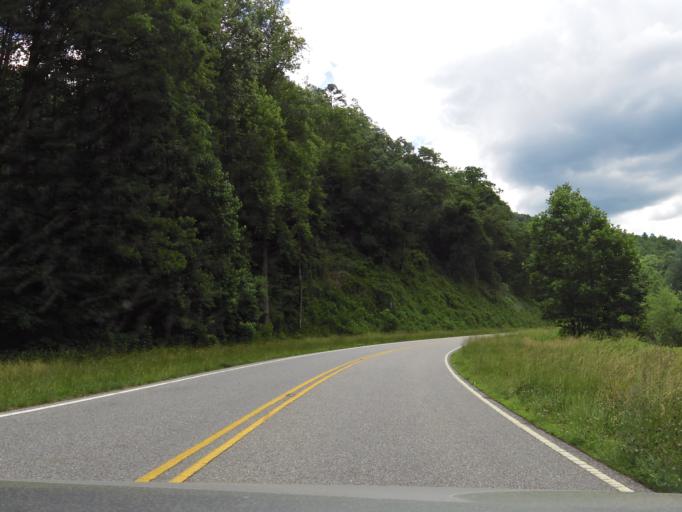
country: US
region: North Carolina
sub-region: Graham County
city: Robbinsville
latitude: 35.4321
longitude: -83.9082
